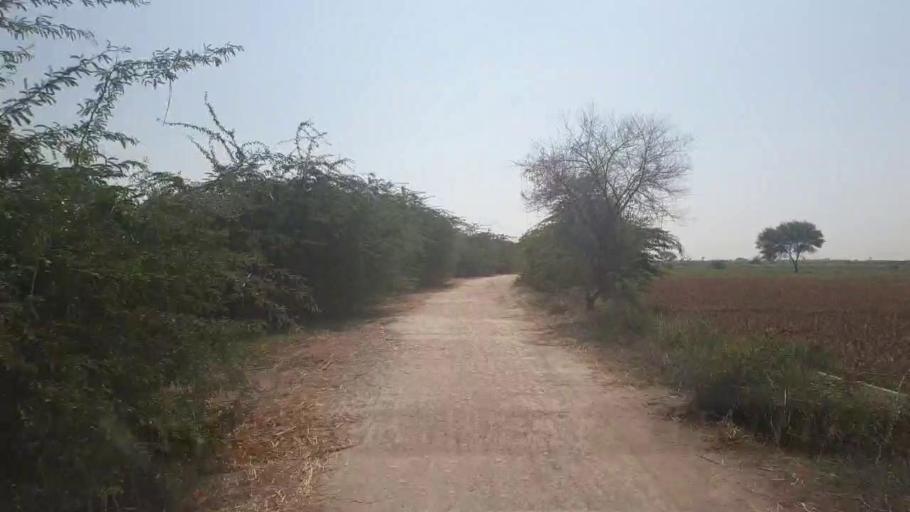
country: PK
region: Sindh
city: Badin
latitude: 24.6442
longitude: 68.9122
